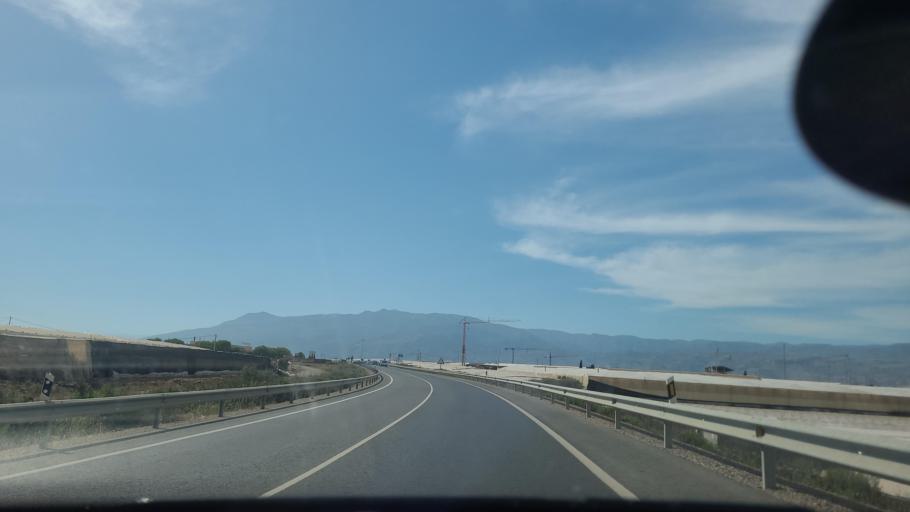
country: ES
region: Andalusia
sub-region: Provincia de Almeria
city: Roquetas de Mar
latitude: 36.7449
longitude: -2.6275
